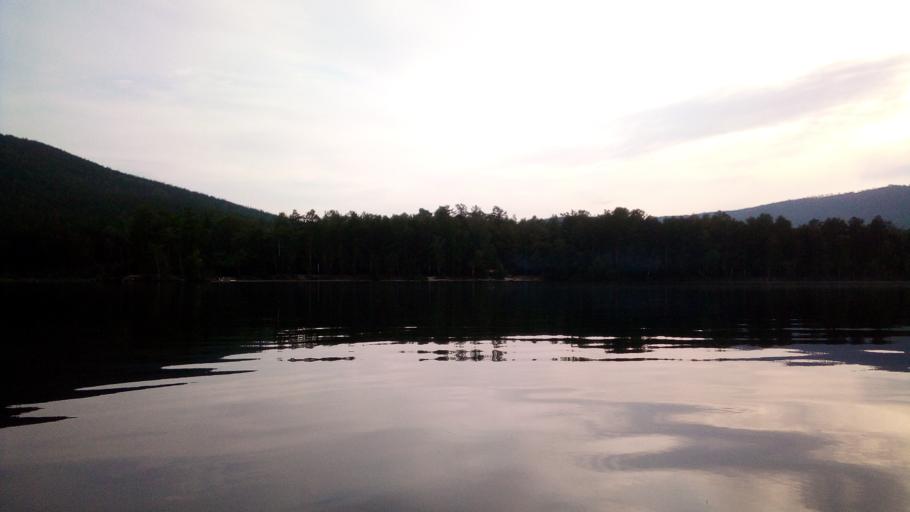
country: RU
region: Chelyabinsk
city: Turgoyak
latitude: 55.1629
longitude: 60.0286
